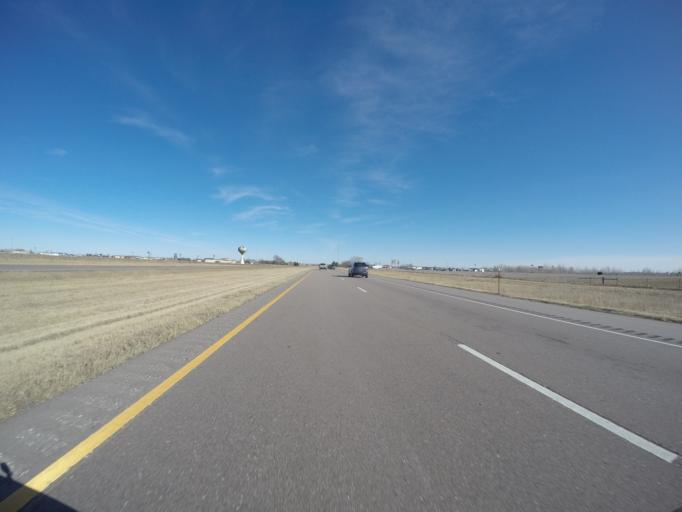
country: US
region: Nebraska
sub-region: York County
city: York
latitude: 40.8212
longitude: -97.6079
